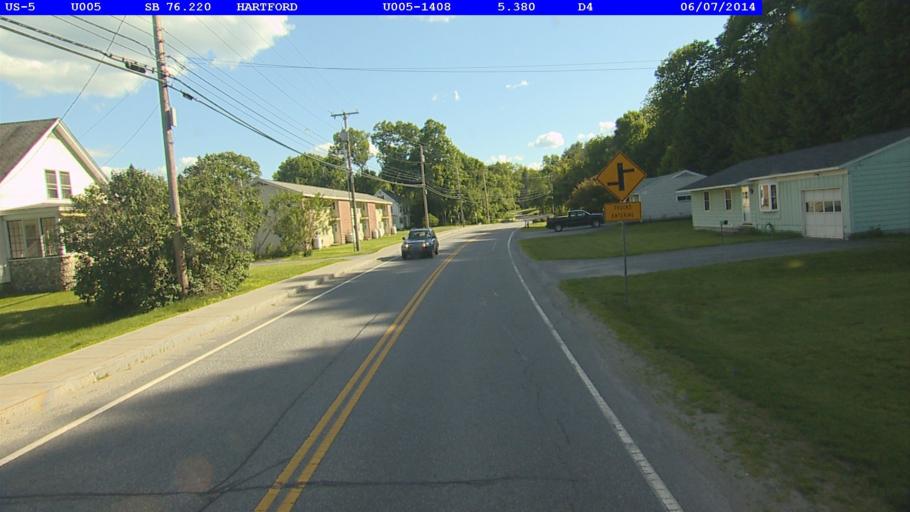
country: US
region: Vermont
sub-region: Windsor County
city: Wilder
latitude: 43.6694
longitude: -72.3106
